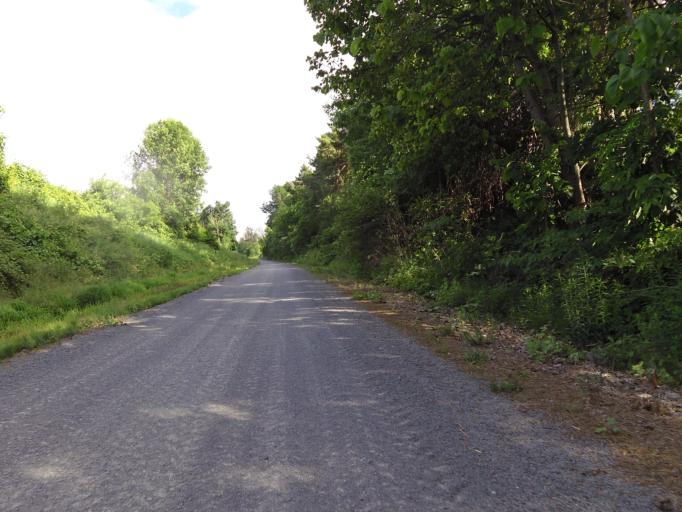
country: CA
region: Ontario
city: Arnprior
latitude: 45.3152
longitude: -76.2840
